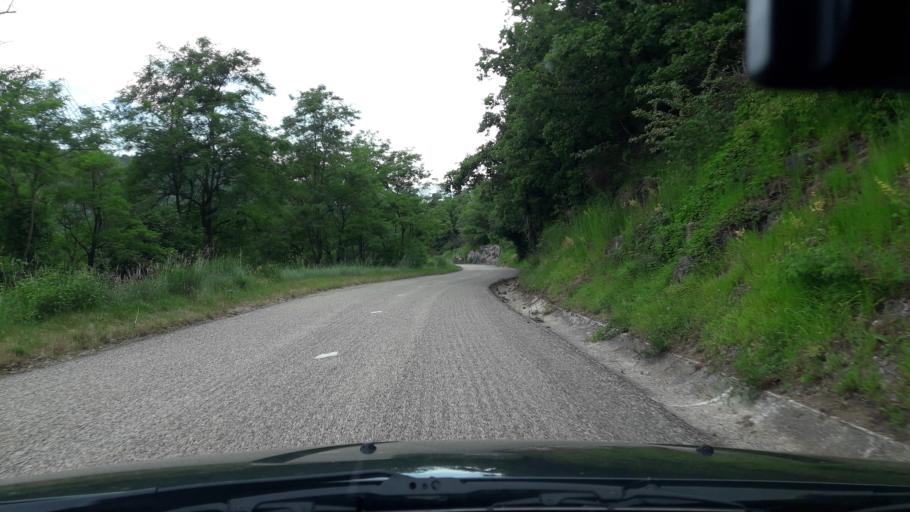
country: FR
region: Rhone-Alpes
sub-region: Departement de l'Ardeche
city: Saint-Priest
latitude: 44.6568
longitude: 4.5256
